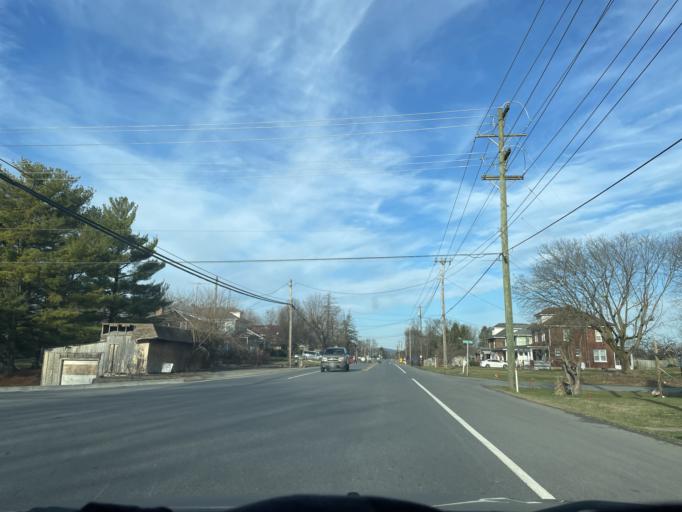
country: US
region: Maryland
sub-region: Washington County
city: Halfway
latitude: 39.6495
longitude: -77.7655
